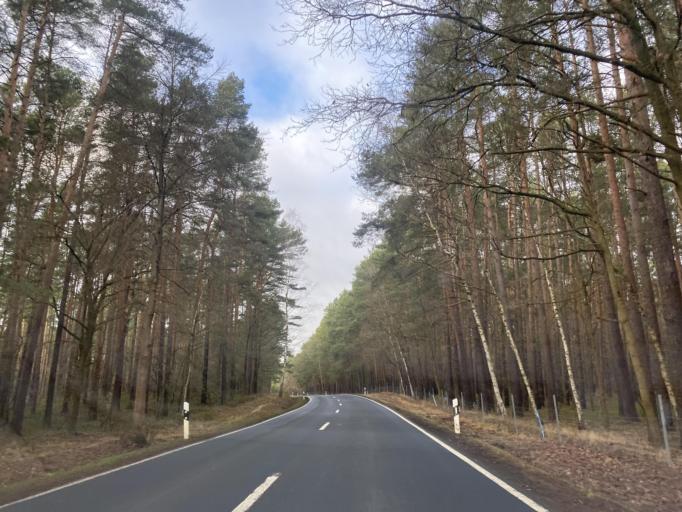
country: PL
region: Lubusz
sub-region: Powiat zarski
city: Leknica
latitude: 51.5040
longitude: 14.8026
